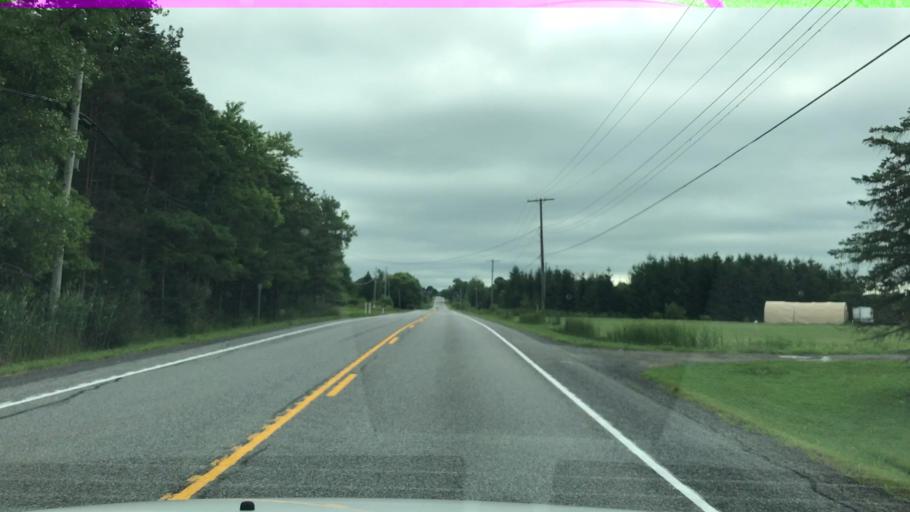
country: US
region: New York
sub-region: Wyoming County
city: Attica
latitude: 42.8360
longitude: -78.3637
